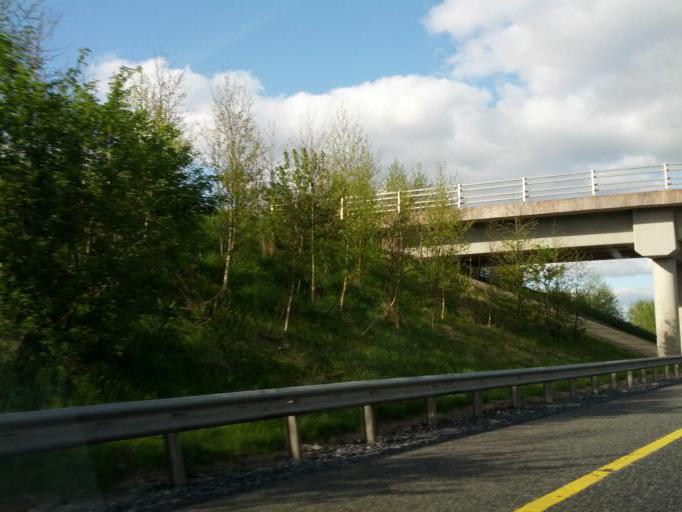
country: IE
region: Leinster
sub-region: An Iarmhi
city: Rochfortbridge
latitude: 53.4272
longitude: -7.2287
